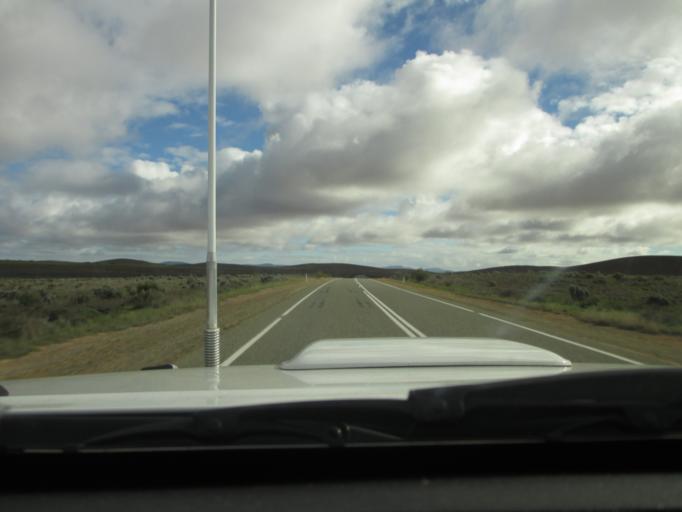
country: AU
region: South Australia
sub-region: Flinders Ranges
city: Quorn
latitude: -32.1573
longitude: 138.5285
